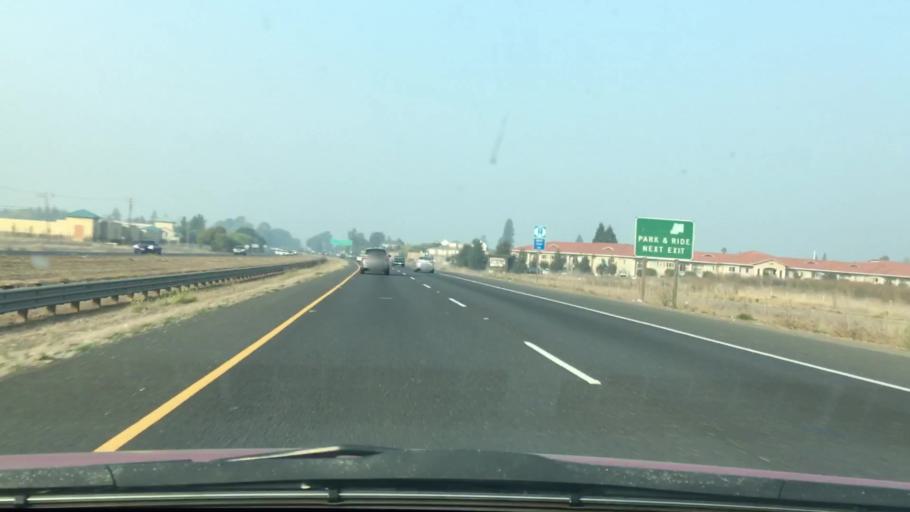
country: US
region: California
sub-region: Napa County
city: Napa
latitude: 38.2733
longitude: -122.2984
